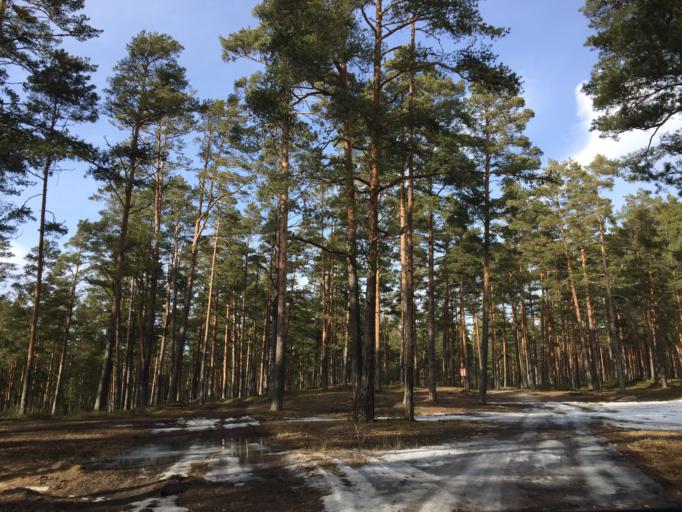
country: EE
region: Paernumaa
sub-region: Paernu linn
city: Parnu
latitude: 58.2278
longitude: 24.5144
